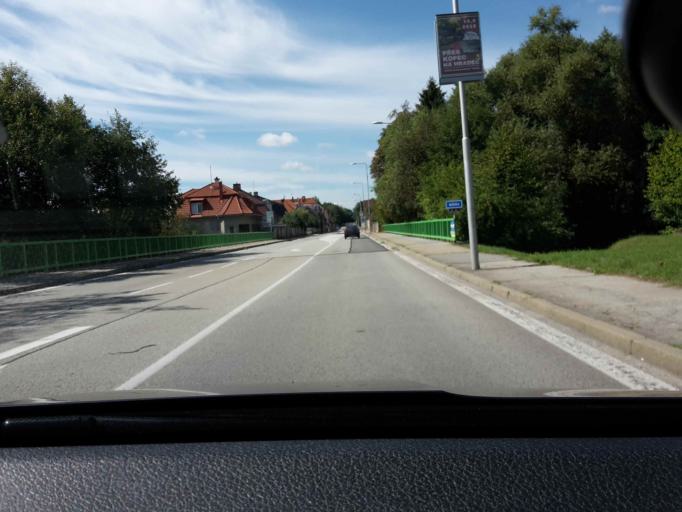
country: CZ
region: Jihocesky
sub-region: Okres Jindrichuv Hradec
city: Jindrichuv Hradec
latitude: 49.1541
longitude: 15.0005
